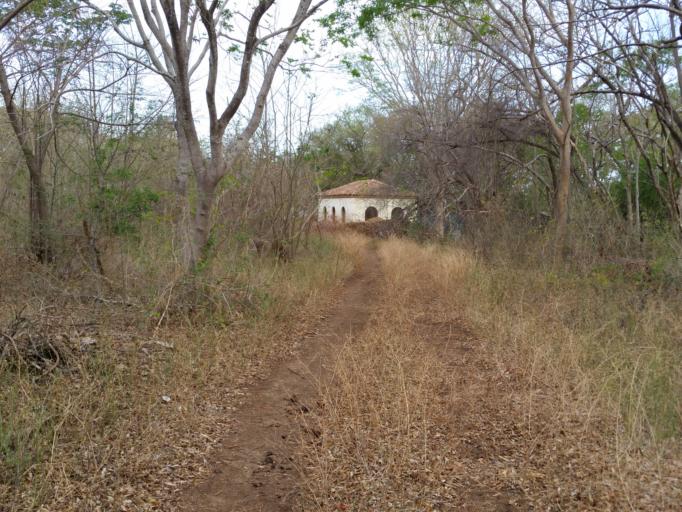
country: NI
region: Rivas
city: Tola
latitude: 11.4409
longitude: -86.0826
